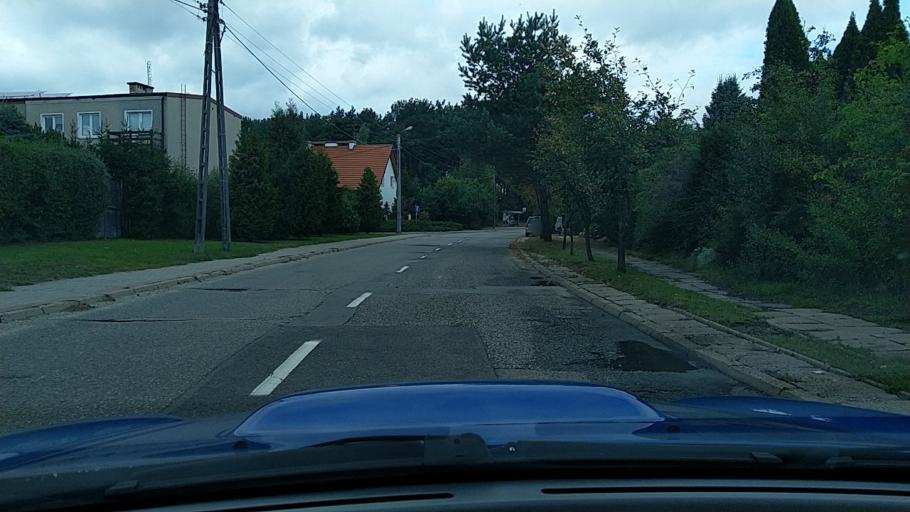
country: PL
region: Warmian-Masurian Voivodeship
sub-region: Olsztyn
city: Kortowo
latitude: 53.7637
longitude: 20.4164
